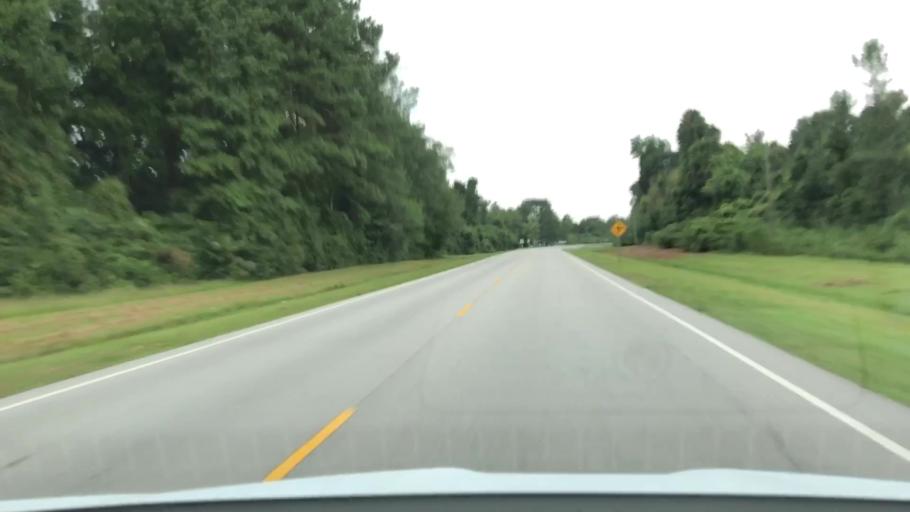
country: US
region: North Carolina
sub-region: Jones County
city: Trenton
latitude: 35.0172
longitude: -77.2991
